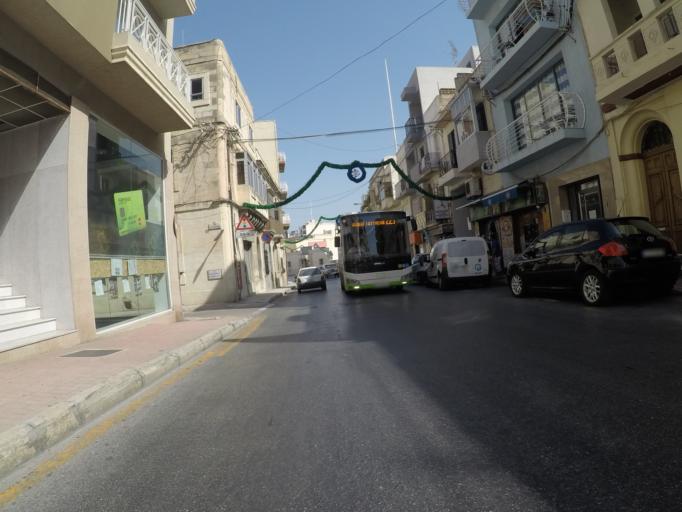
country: MT
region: Saint Paul's Bay
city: San Pawl il-Bahar
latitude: 35.9484
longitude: 14.4040
